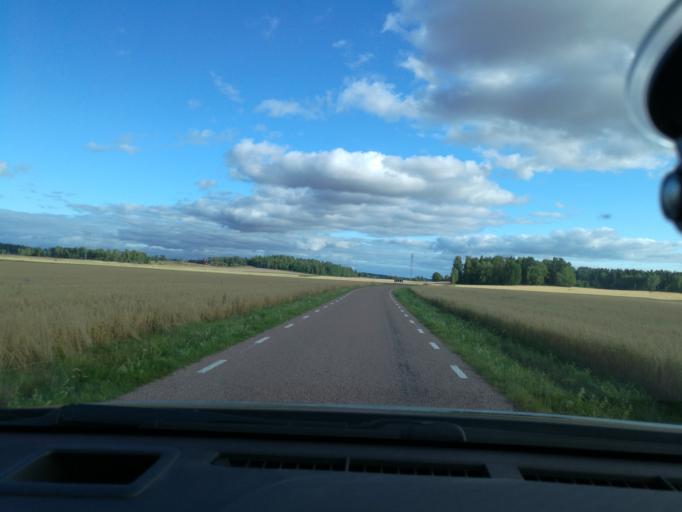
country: SE
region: Vaestmanland
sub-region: Kopings Kommun
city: Koping
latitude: 59.5563
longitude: 16.0970
